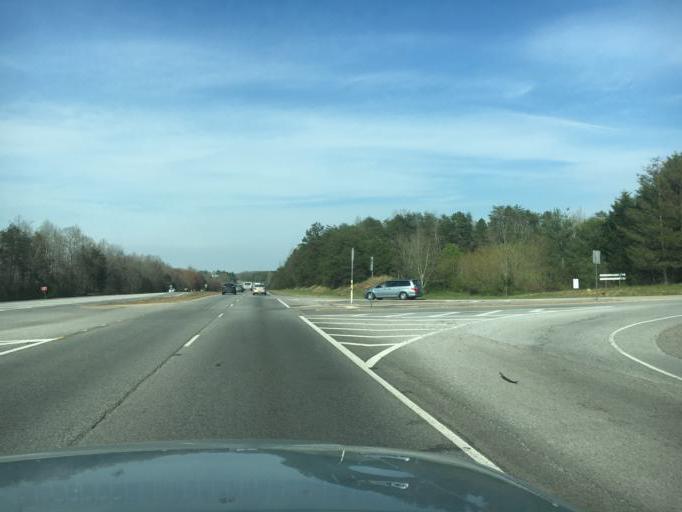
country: US
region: Georgia
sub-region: Habersham County
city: Raoul
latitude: 34.4677
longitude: -83.5998
